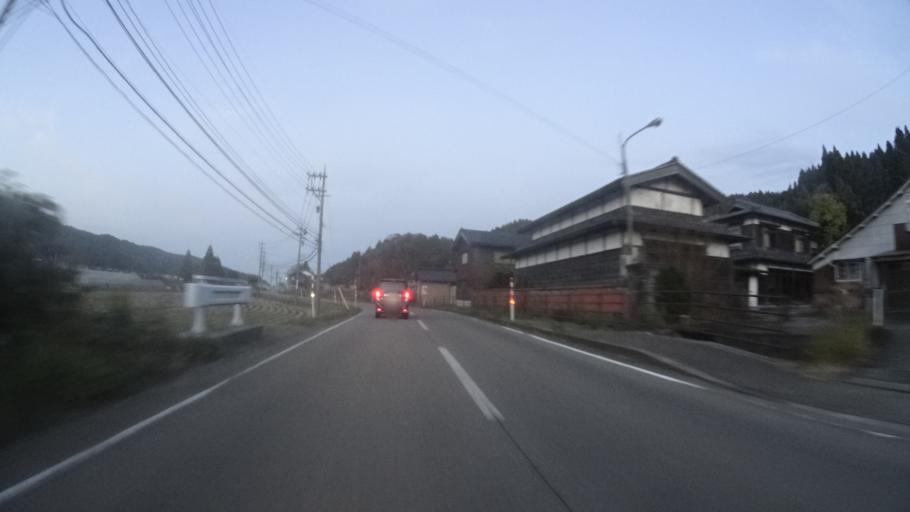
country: JP
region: Ishikawa
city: Nanao
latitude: 37.3697
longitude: 136.8749
